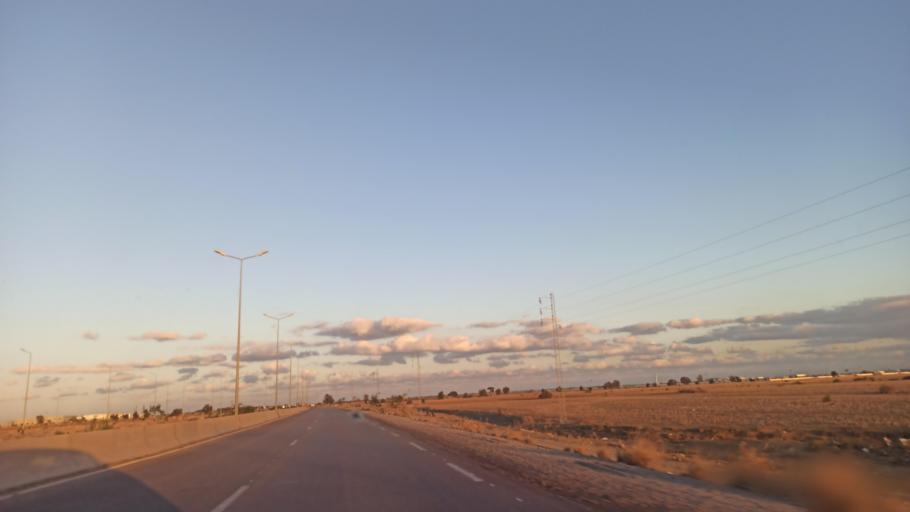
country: TN
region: Susah
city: Harqalah
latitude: 36.0998
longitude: 10.3800
